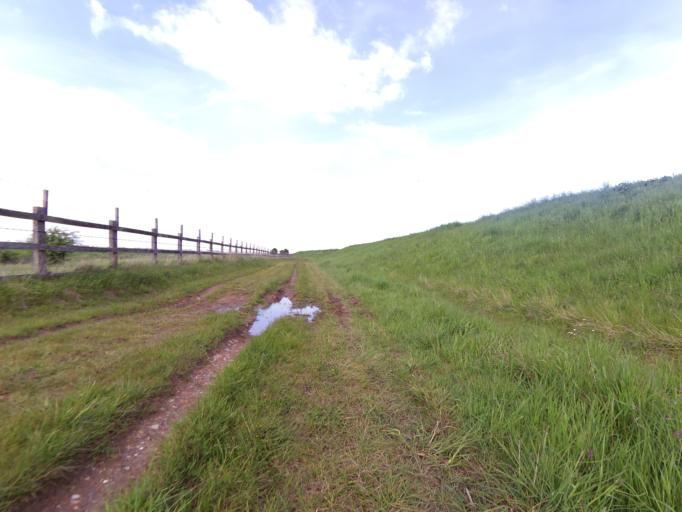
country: GB
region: England
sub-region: Norfolk
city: Great Yarmouth
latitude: 52.6088
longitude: 1.6796
